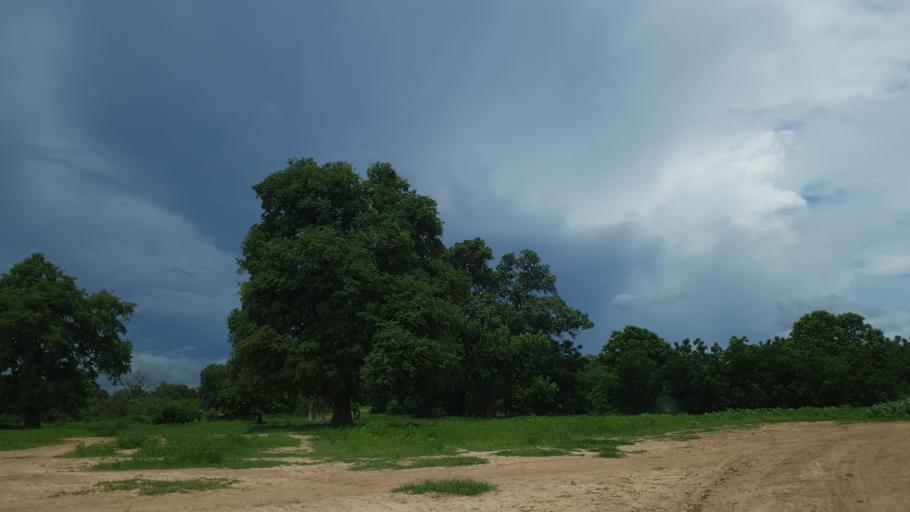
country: ML
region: Koulikoro
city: Kolokani
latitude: 13.5405
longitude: -8.0699
